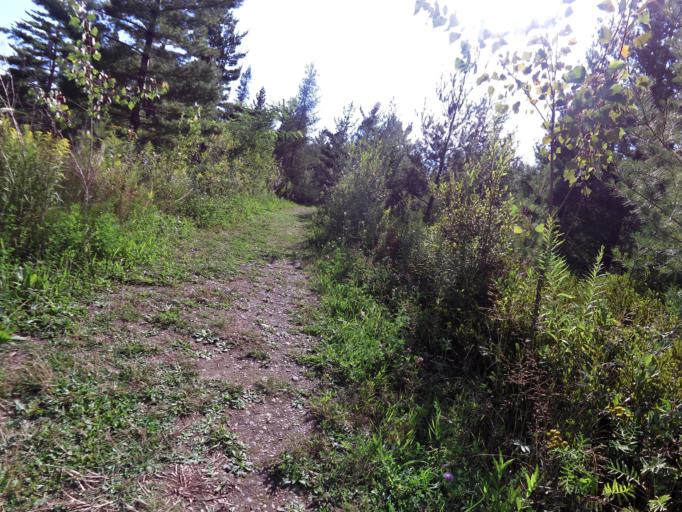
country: CA
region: Ontario
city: Tobermory
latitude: 45.2305
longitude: -81.6452
